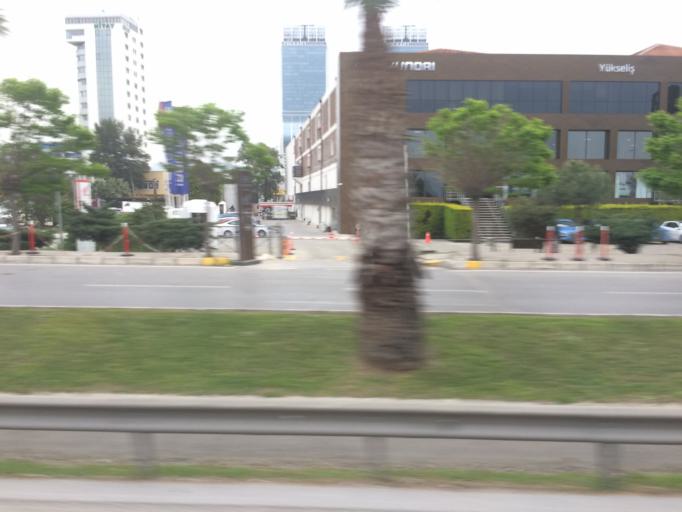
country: TR
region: Izmir
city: Izmir
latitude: 38.4513
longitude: 27.1697
